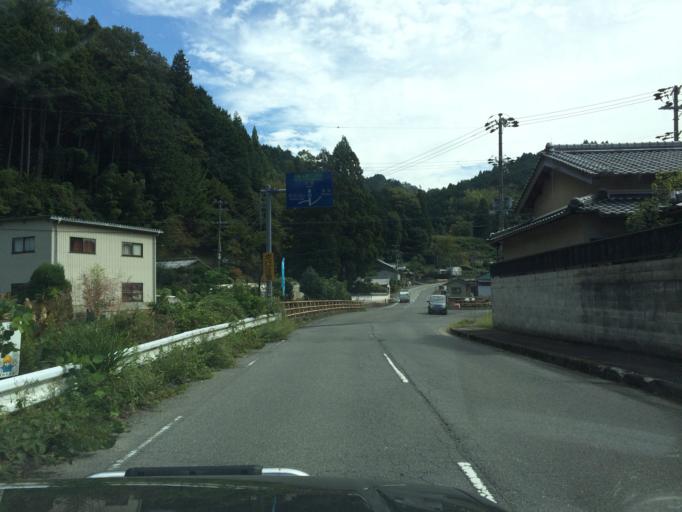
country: JP
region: Mie
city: Nabari
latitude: 34.6801
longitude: 135.9770
